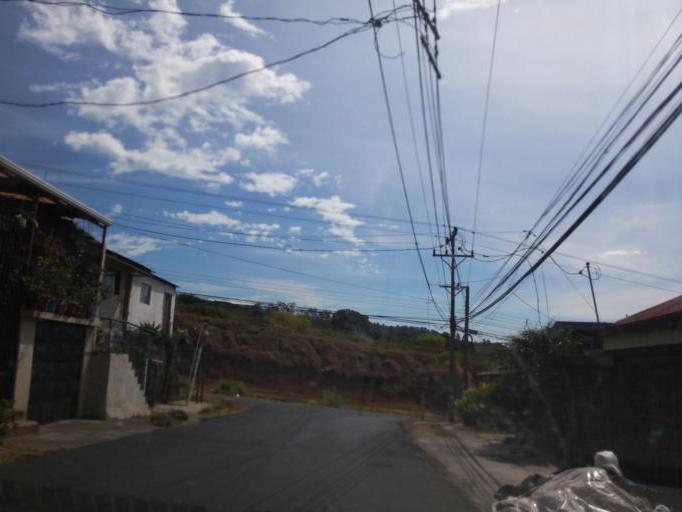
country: CR
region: Alajuela
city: Sabanilla
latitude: 10.0464
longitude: -84.2125
